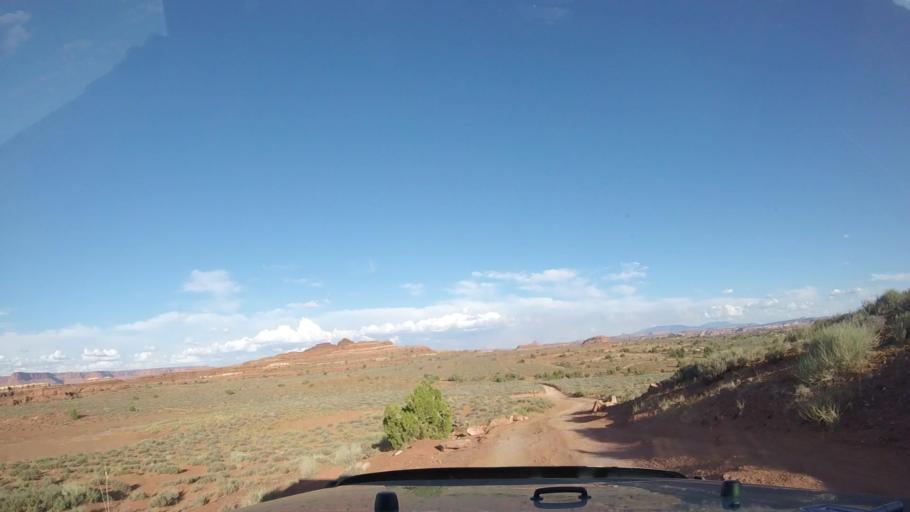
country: US
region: Utah
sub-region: Grand County
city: Moab
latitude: 38.2129
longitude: -109.7899
